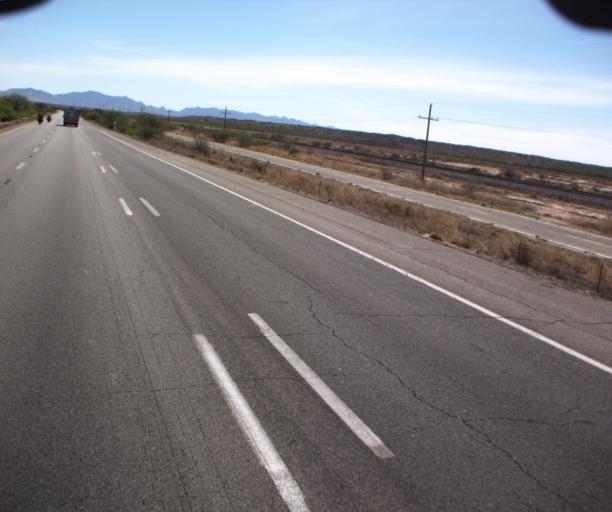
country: US
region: Arizona
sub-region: Cochise County
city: Benson
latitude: 31.9651
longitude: -110.2655
